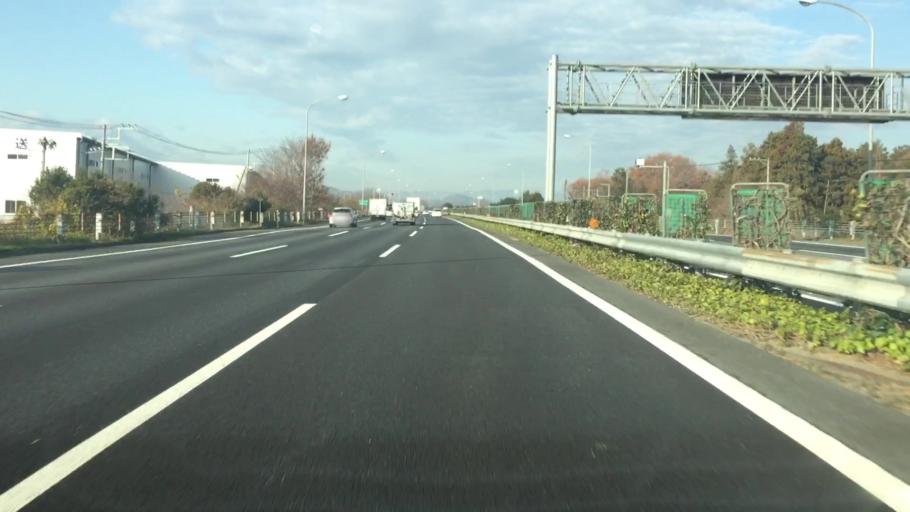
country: JP
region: Saitama
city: Sakado
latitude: 36.0441
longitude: 139.3592
